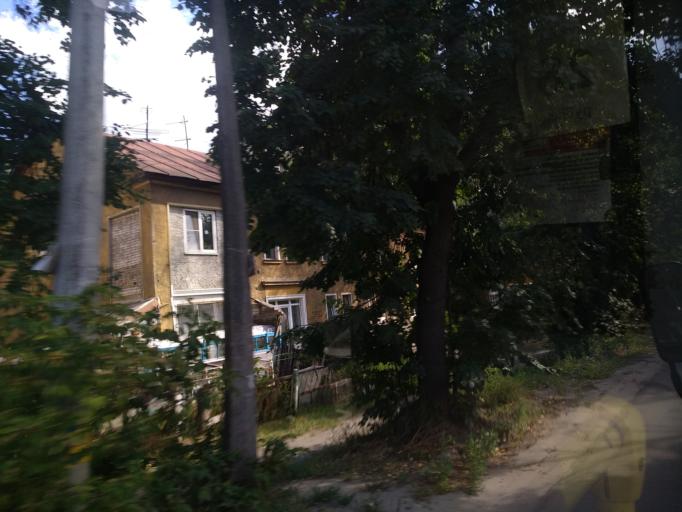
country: RU
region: Nizjnij Novgorod
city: Gorbatovka
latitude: 56.2472
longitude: 43.8291
